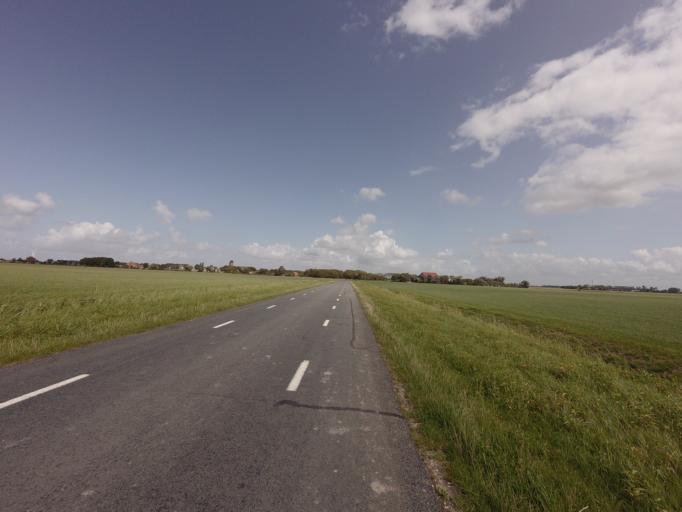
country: NL
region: Friesland
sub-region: Sudwest Fryslan
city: Makkum
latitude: 53.1095
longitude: 5.4365
